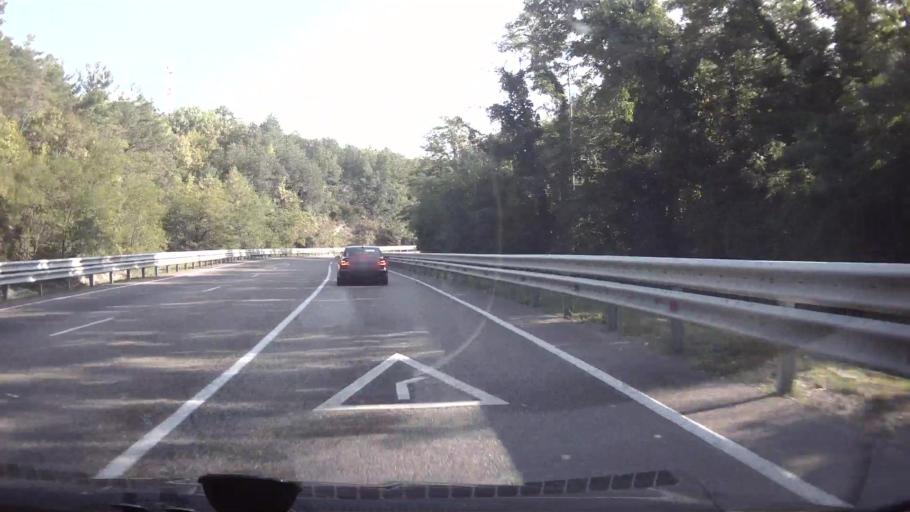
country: RU
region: Krasnodarskiy
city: Shepsi
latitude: 44.0266
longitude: 39.1581
